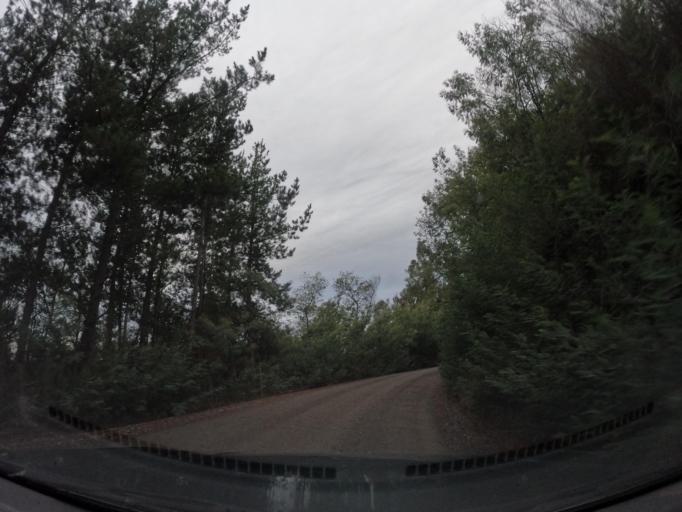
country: CL
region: Biobio
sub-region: Provincia de Concepcion
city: Chiguayante
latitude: -37.0107
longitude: -72.8700
